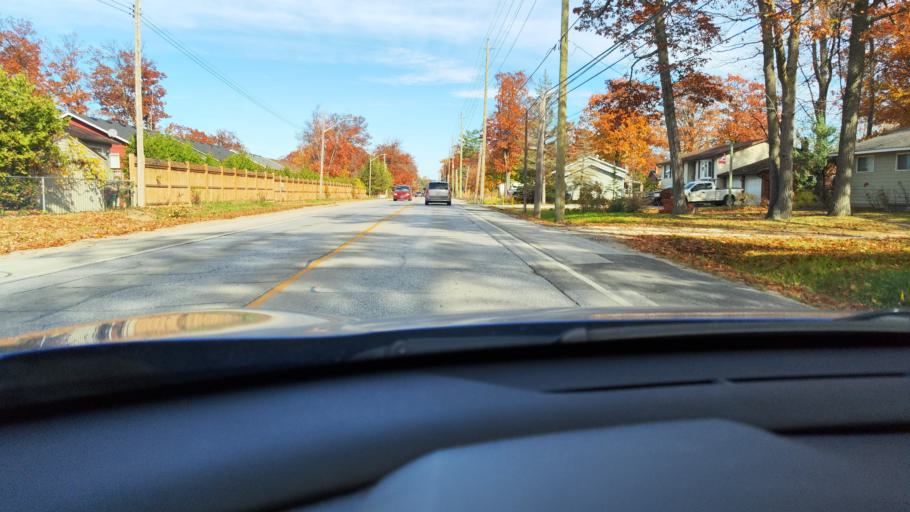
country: CA
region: Ontario
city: Wasaga Beach
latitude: 44.5057
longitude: -80.0316
